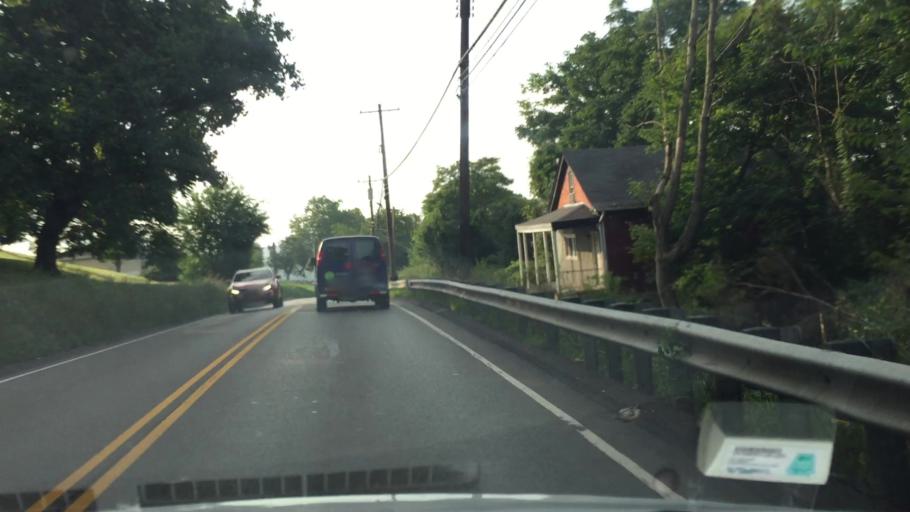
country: US
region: Pennsylvania
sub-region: Allegheny County
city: McKees Rocks
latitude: 40.4704
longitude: -80.0907
